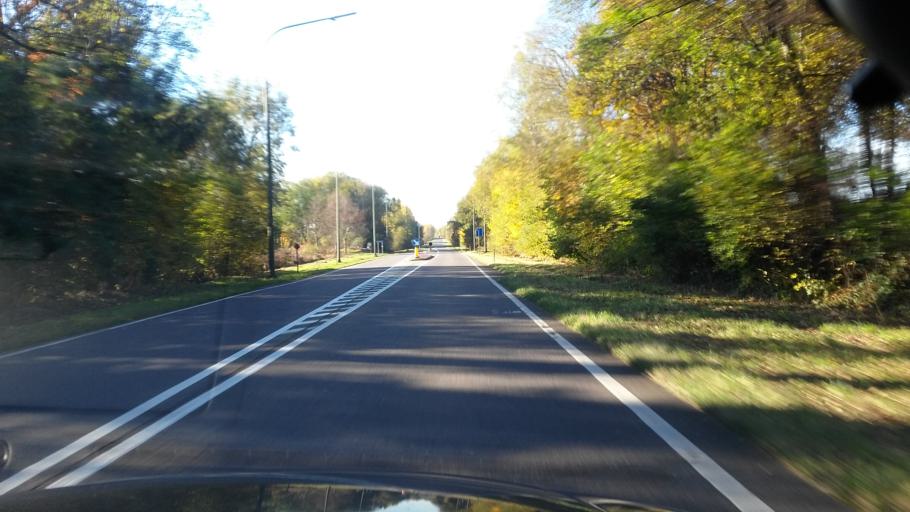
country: BE
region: Wallonia
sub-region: Province du Luxembourg
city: Etalle
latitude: 49.6723
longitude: 5.6427
